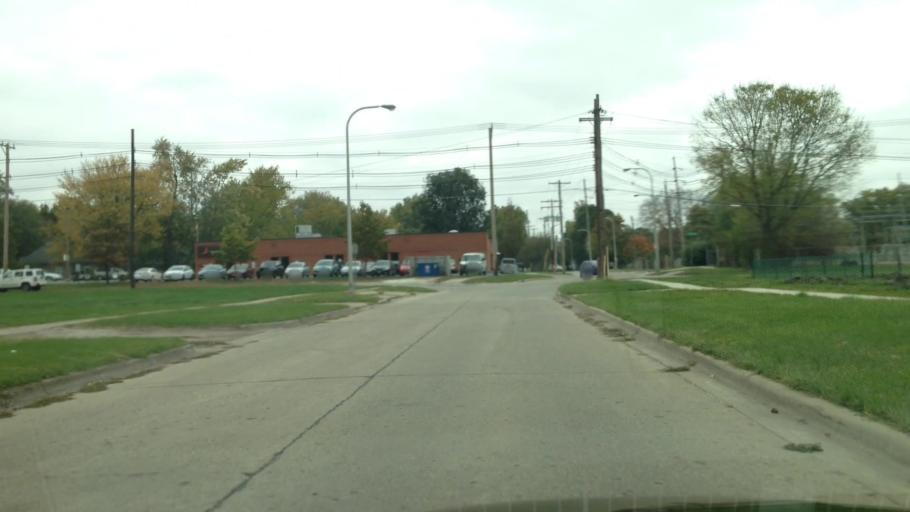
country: US
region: Illinois
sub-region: Champaign County
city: Champaign
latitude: 40.1228
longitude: -88.2412
